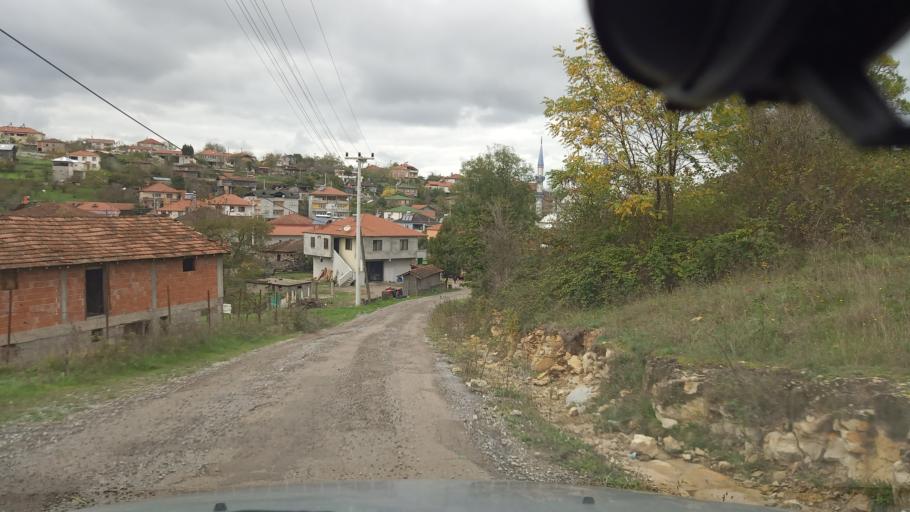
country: TR
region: Sakarya
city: Karasu
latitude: 41.0924
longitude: 30.5843
